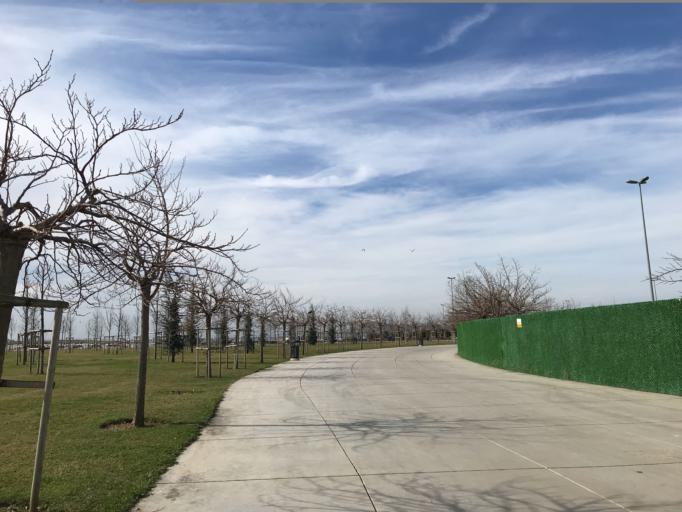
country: TR
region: Istanbul
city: Maltepe
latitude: 40.9306
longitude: 29.1153
